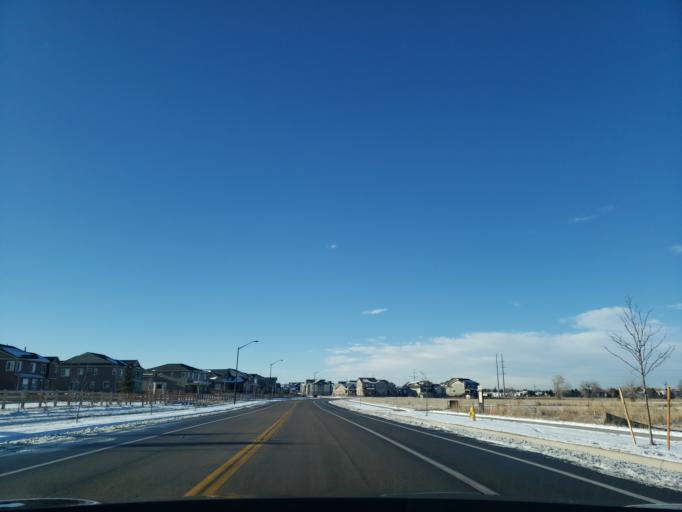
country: US
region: Colorado
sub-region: Larimer County
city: Fort Collins
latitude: 40.5540
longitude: -105.0264
